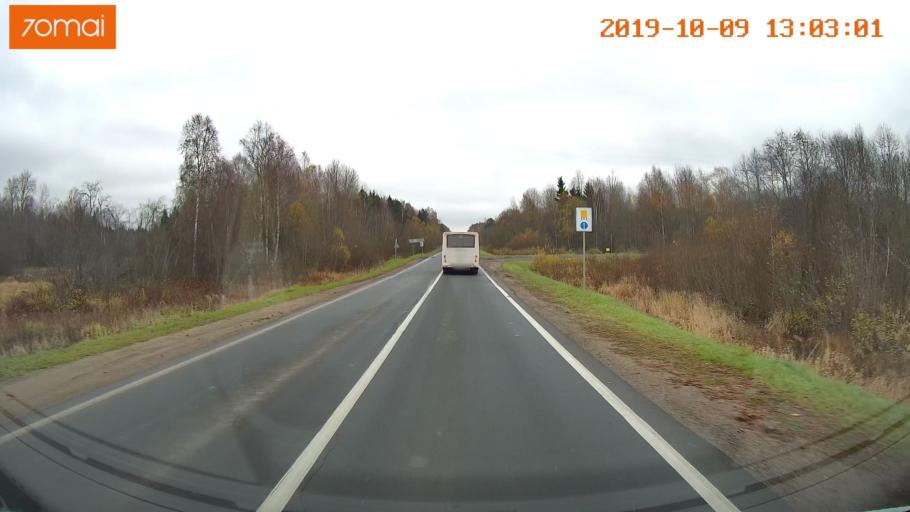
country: RU
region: Jaroslavl
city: Lyubim
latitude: 58.3598
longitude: 40.5157
